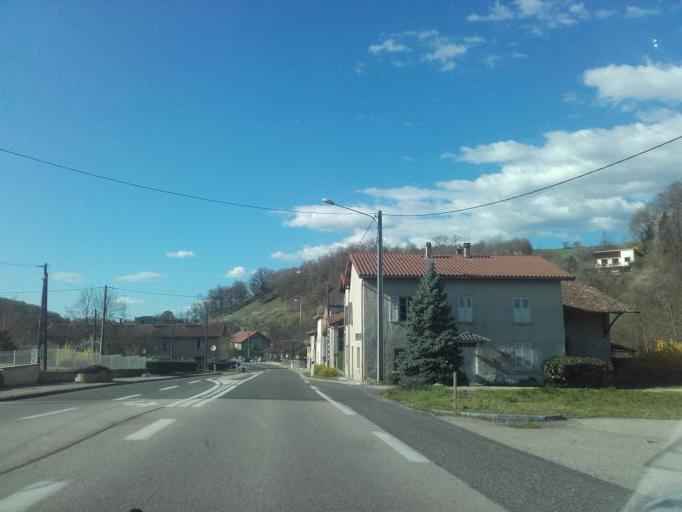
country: FR
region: Rhone-Alpes
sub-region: Departement de l'Isere
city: Nivolas-Vermelle
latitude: 45.5488
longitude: 5.3093
